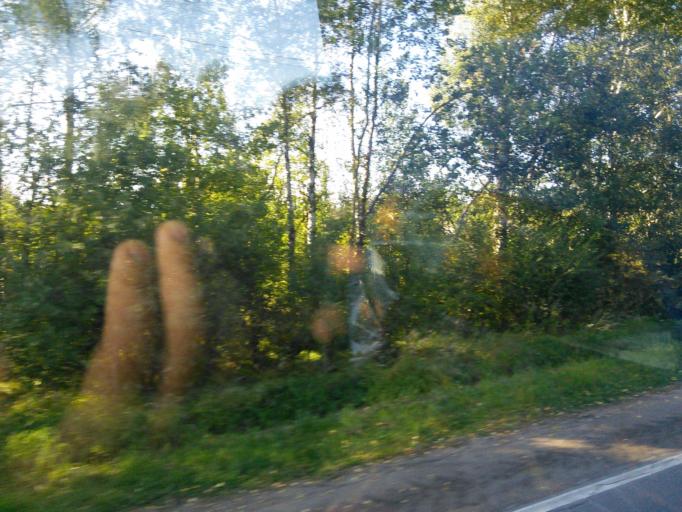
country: RU
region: Jaroslavl
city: Rybinsk
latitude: 58.2855
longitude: 38.8651
